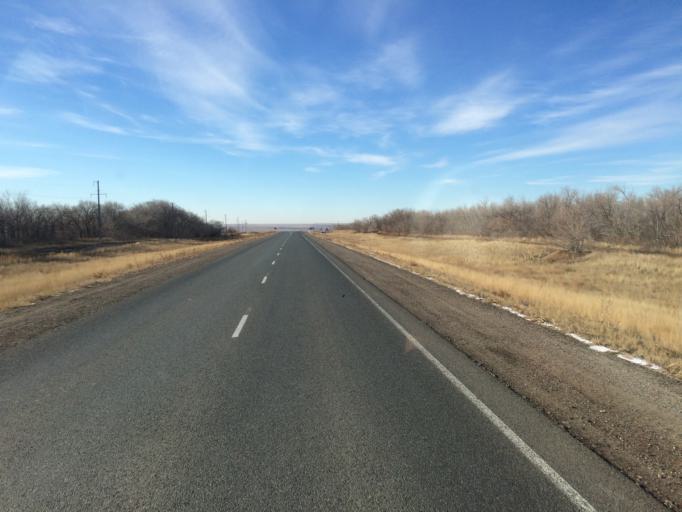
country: KZ
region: Aqtoebe
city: Aqtobe
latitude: 50.2475
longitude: 56.7942
